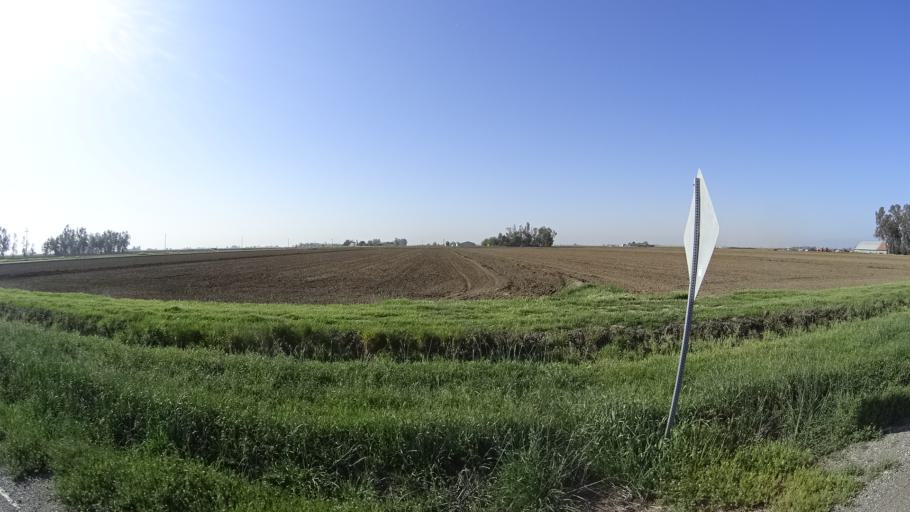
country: US
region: California
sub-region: Glenn County
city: Willows
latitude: 39.5748
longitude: -122.1094
